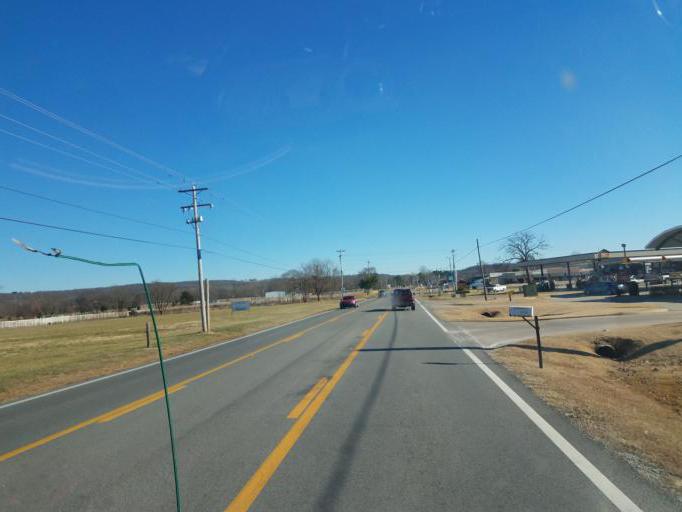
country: US
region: Arkansas
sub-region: Washington County
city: Elkins
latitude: 36.0301
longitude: -94.0292
